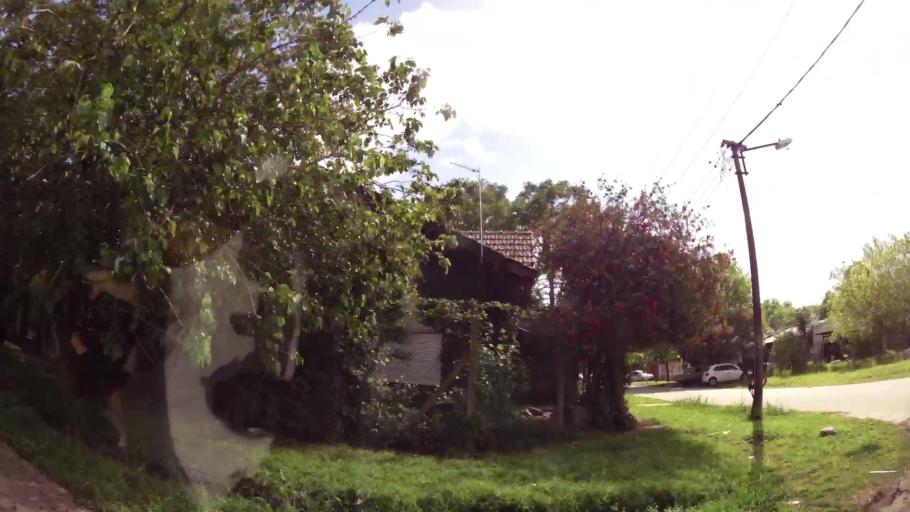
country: AR
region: Buenos Aires
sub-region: Partido de Quilmes
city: Quilmes
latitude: -34.8366
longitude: -58.1716
